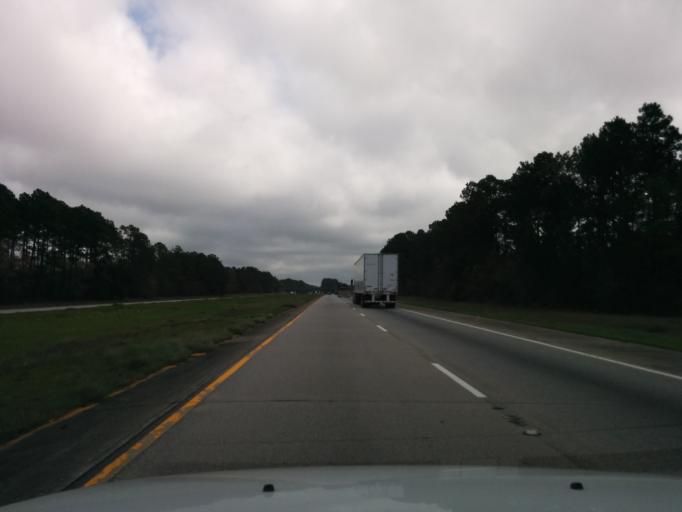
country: US
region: Georgia
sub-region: Toombs County
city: Lyons
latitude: 32.3887
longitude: -82.2751
